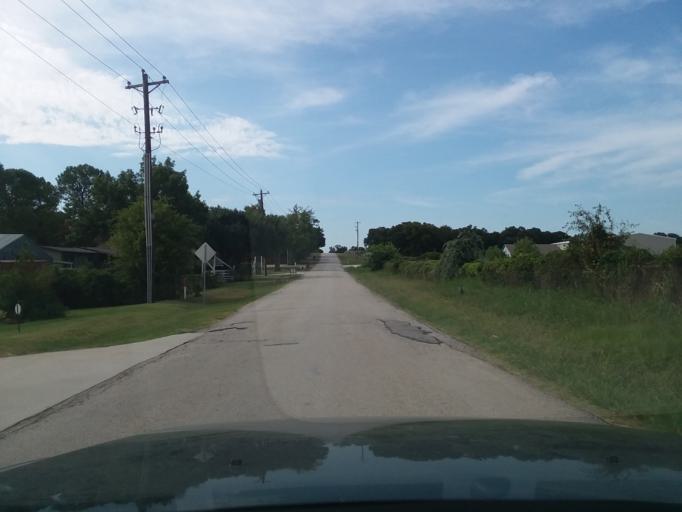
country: US
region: Texas
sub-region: Denton County
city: Copper Canyon
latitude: 33.1163
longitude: -97.1311
